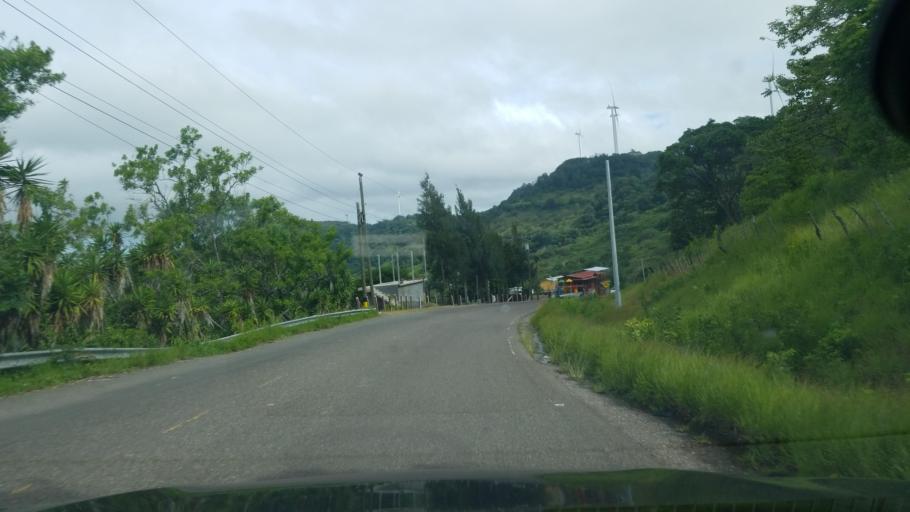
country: HN
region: Choluteca
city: Corpus
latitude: 13.3637
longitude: -86.9299
